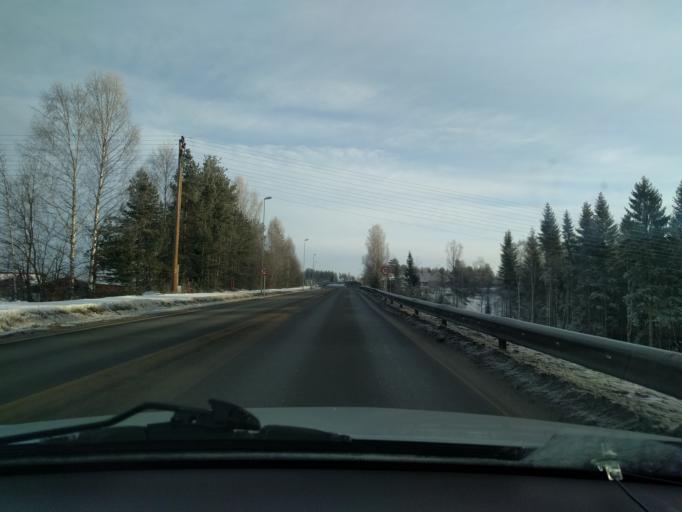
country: NO
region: Hedmark
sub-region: Elverum
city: Elverum
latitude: 60.8959
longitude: 11.5844
